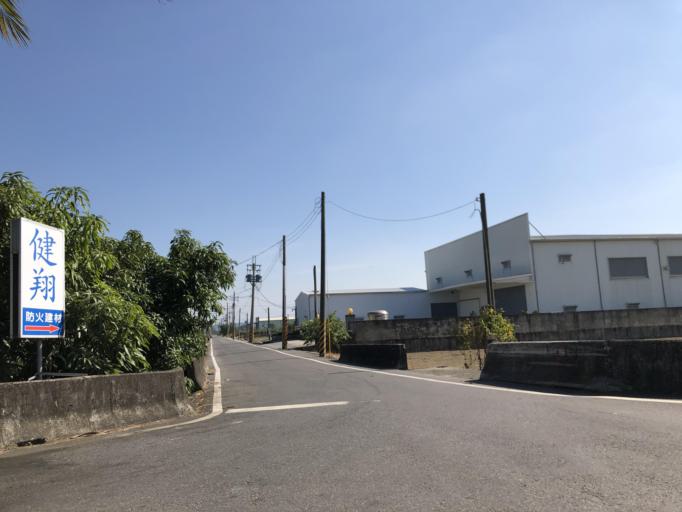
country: TW
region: Taiwan
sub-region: Tainan
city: Tainan
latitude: 23.0103
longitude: 120.2872
